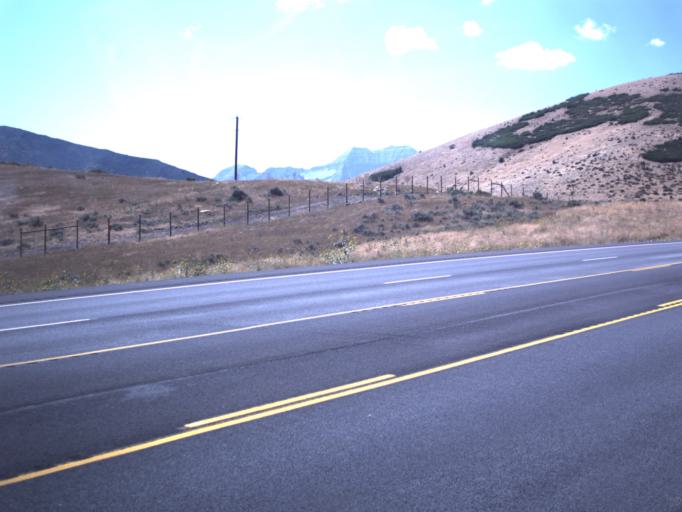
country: US
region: Utah
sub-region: Wasatch County
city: Midway
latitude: 40.4150
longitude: -111.4834
